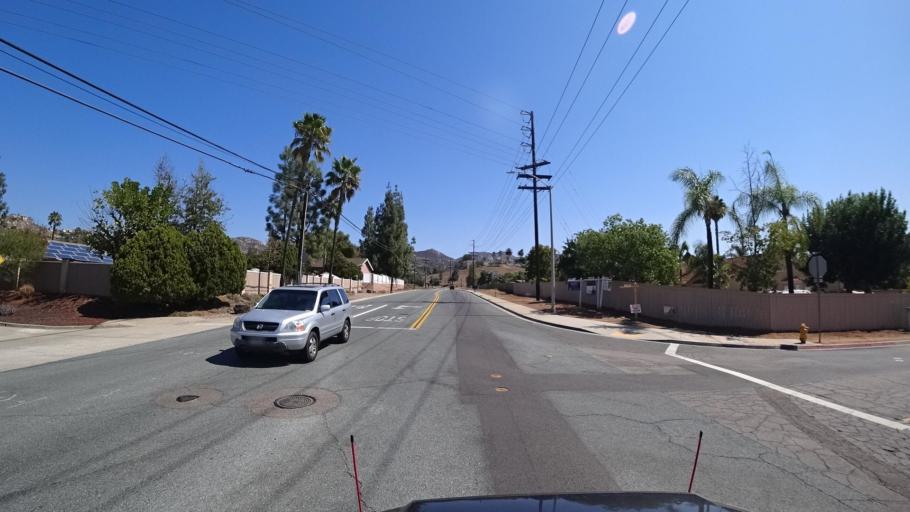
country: US
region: California
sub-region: San Diego County
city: Granite Hills
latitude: 32.8002
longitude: -116.9098
